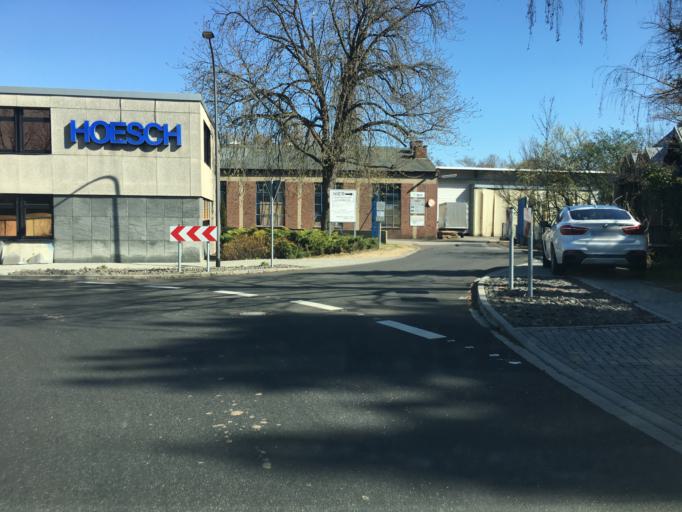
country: DE
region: North Rhine-Westphalia
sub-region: Regierungsbezirk Koln
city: Kreuzau
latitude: 50.7516
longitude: 6.4806
